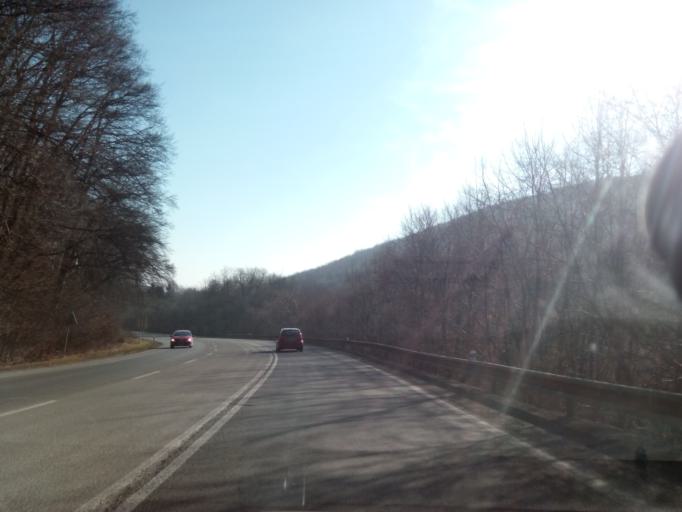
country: SK
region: Kosicky
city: Secovce
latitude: 48.7345
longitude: 21.5496
